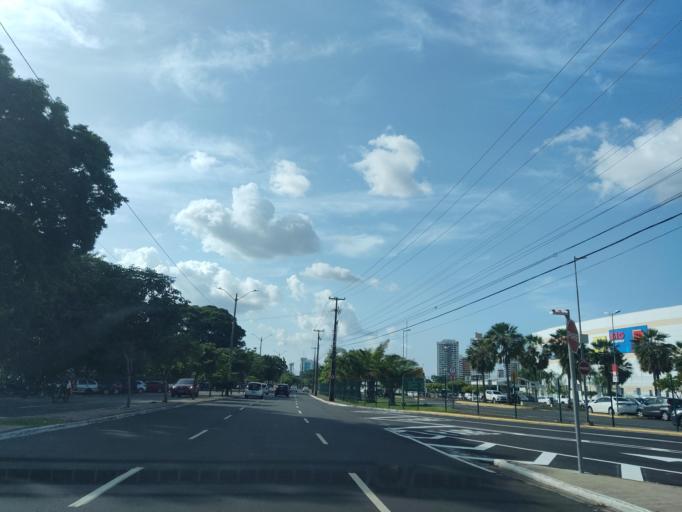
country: BR
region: Piaui
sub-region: Teresina
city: Teresina
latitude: -5.0855
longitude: -42.7912
